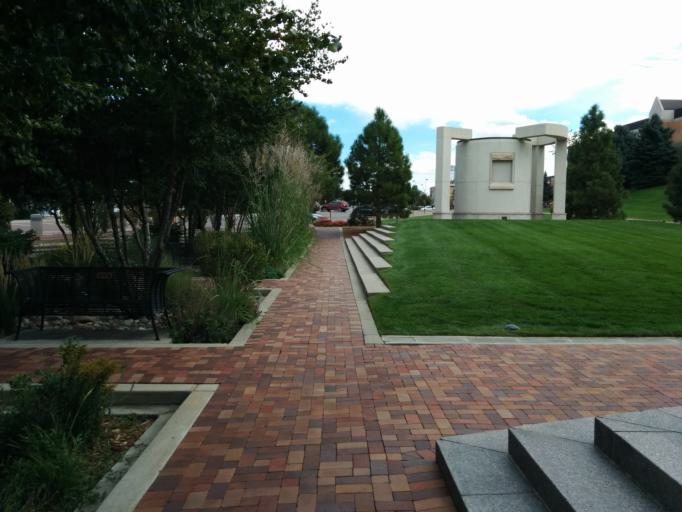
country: US
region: Colorado
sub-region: Arapahoe County
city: Glendale
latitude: 39.6832
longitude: -104.9632
